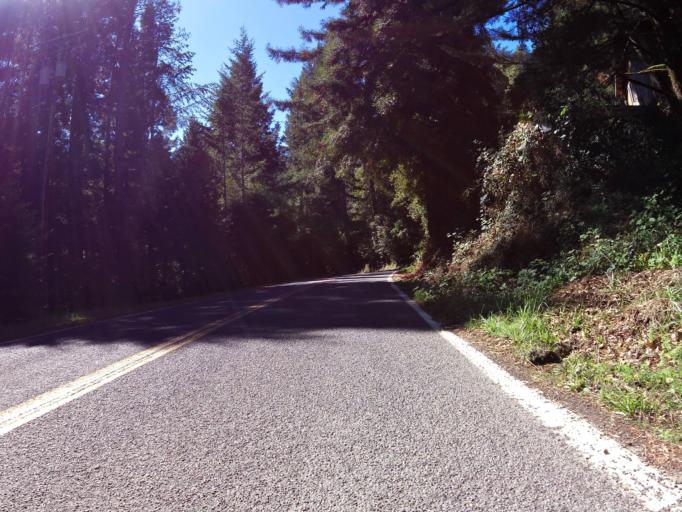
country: US
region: California
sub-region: Humboldt County
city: Redway
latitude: 39.8146
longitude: -123.7868
